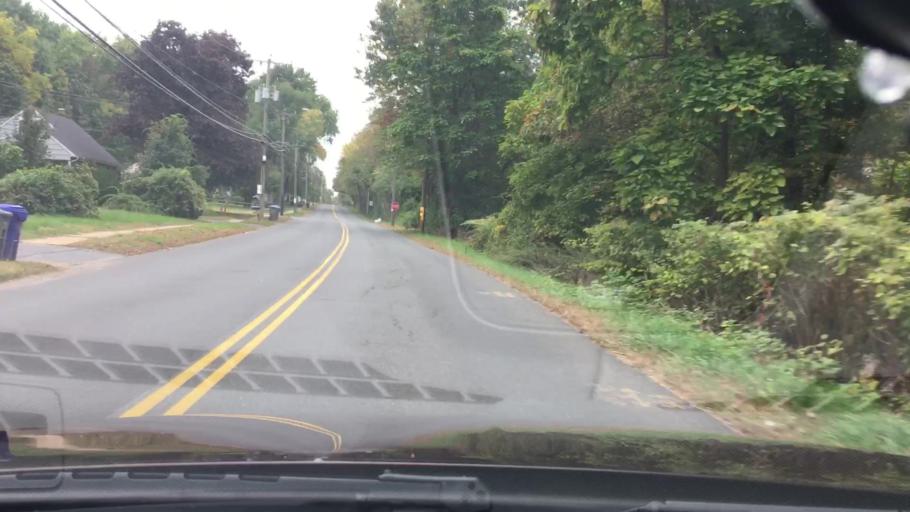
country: US
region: Connecticut
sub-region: Hartford County
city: Hazardville
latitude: 41.9989
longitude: -72.5150
